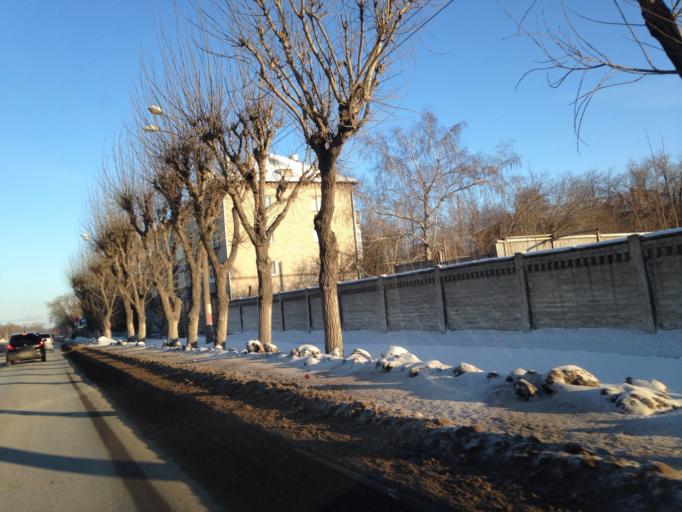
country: RU
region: Ulyanovsk
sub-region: Ulyanovskiy Rayon
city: Ulyanovsk
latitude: 54.2871
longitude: 48.3616
